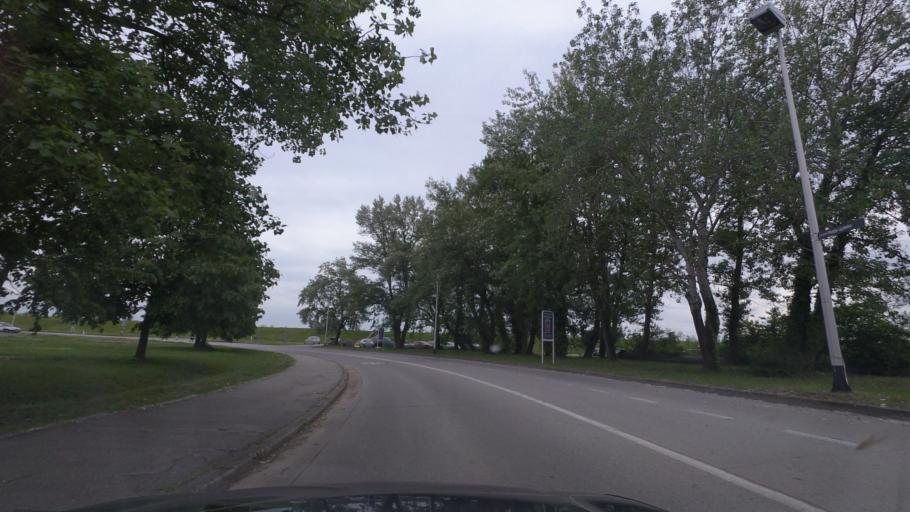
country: HR
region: Grad Zagreb
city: Jankomir
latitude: 45.7802
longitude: 15.9078
